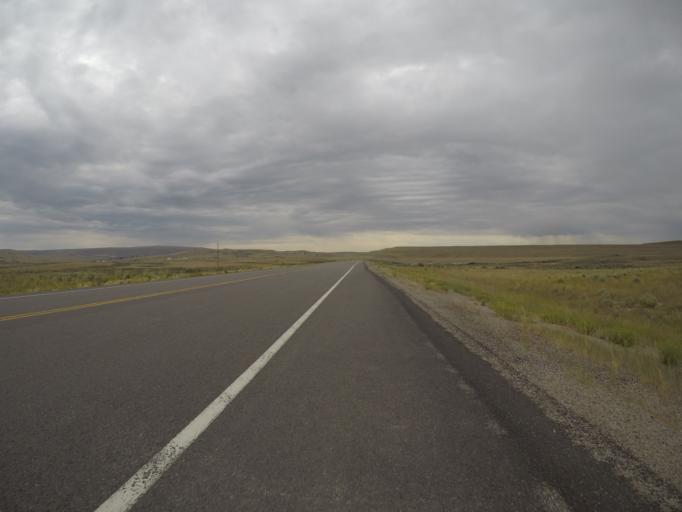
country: US
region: Wyoming
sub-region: Lincoln County
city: Kemmerer
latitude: 41.8010
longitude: -110.5989
